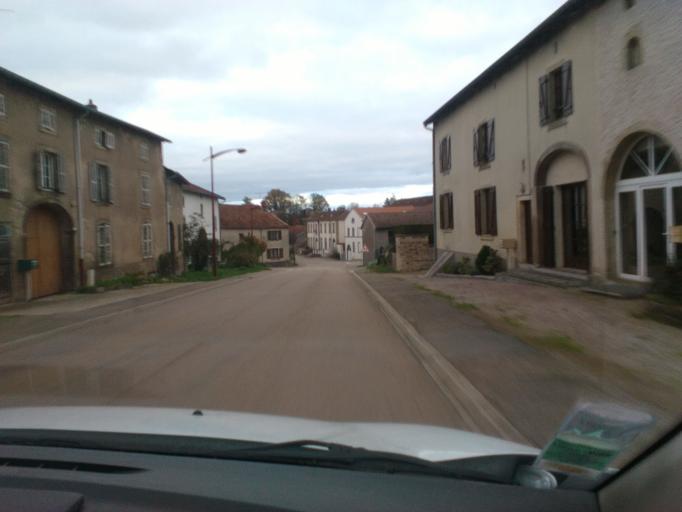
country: FR
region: Lorraine
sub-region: Departement des Vosges
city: Darnieulles
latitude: 48.2420
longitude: 6.3382
